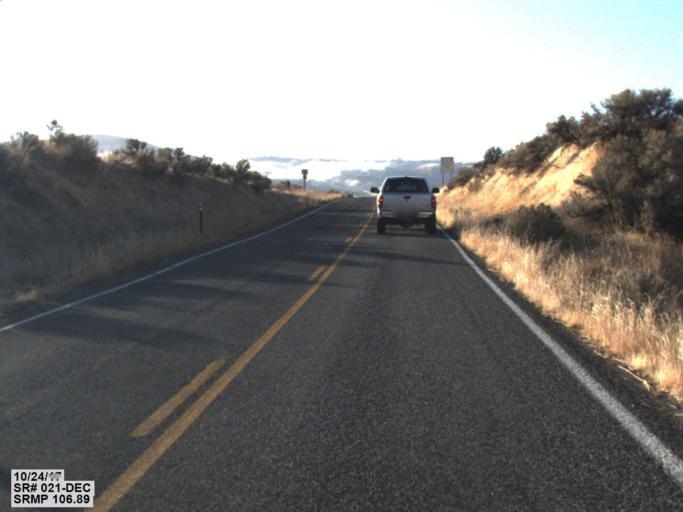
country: US
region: Washington
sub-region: Okanogan County
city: Coulee Dam
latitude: 47.9500
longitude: -118.6904
